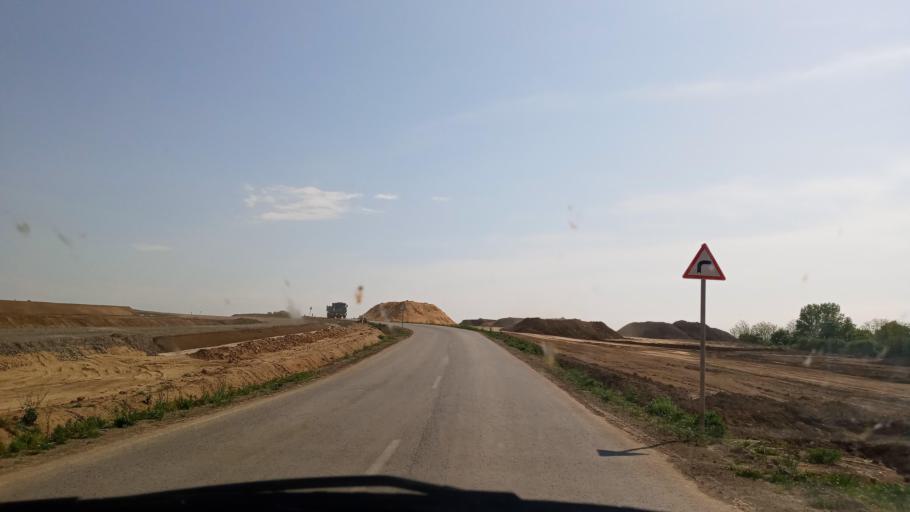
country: HU
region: Baranya
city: Boly
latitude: 45.9534
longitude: 18.5600
